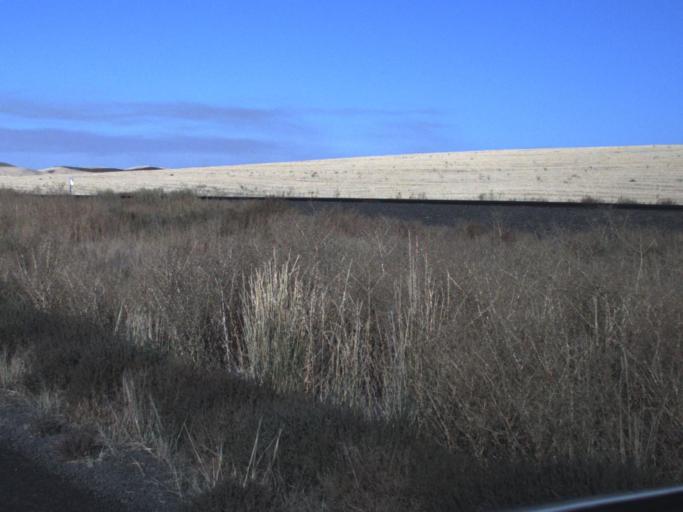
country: US
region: Washington
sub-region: Walla Walla County
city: Walla Walla
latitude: 46.1619
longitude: -118.3793
